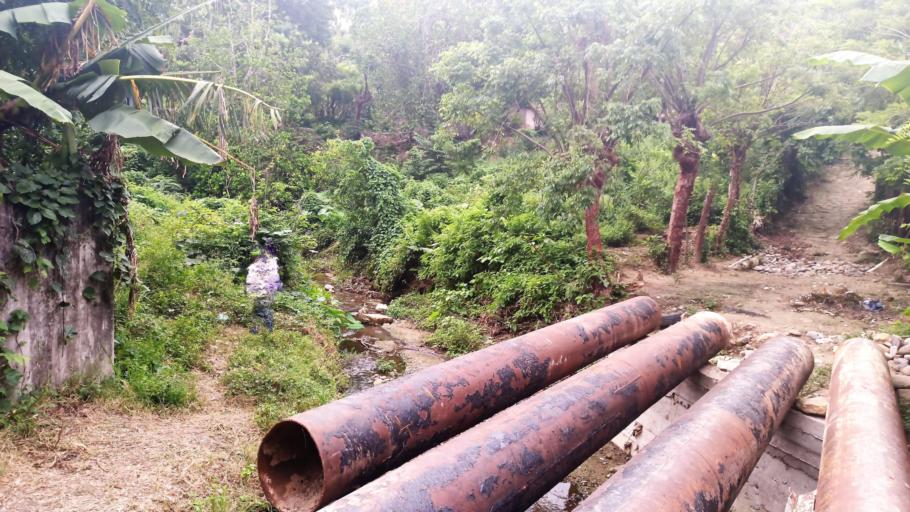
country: MX
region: Veracruz
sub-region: Papantla
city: Residencial Tajin
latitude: 20.6001
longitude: -97.3353
